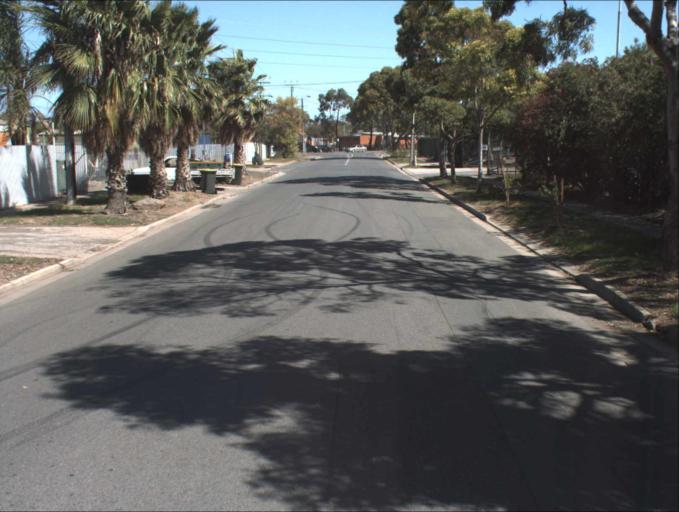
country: AU
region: South Australia
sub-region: Port Adelaide Enfield
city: Enfield
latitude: -34.8368
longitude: 138.5861
